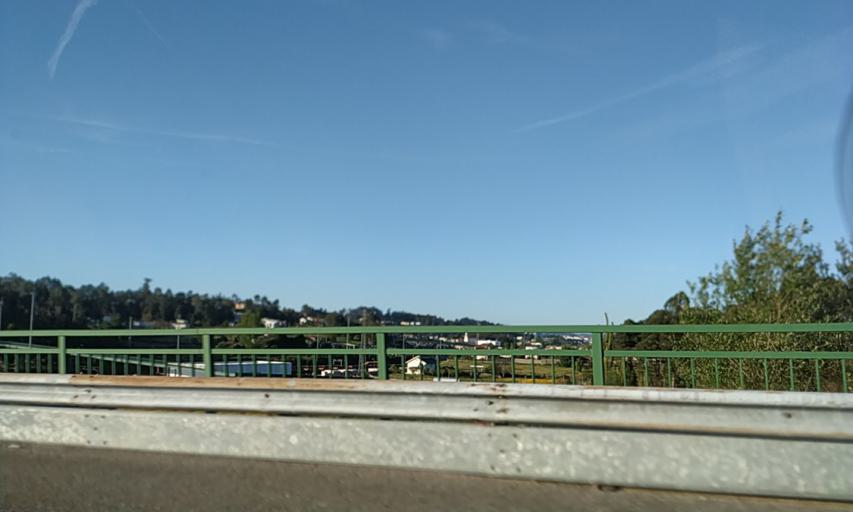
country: PT
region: Braga
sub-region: Braga
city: Oliveira
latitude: 41.5134
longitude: -8.4734
